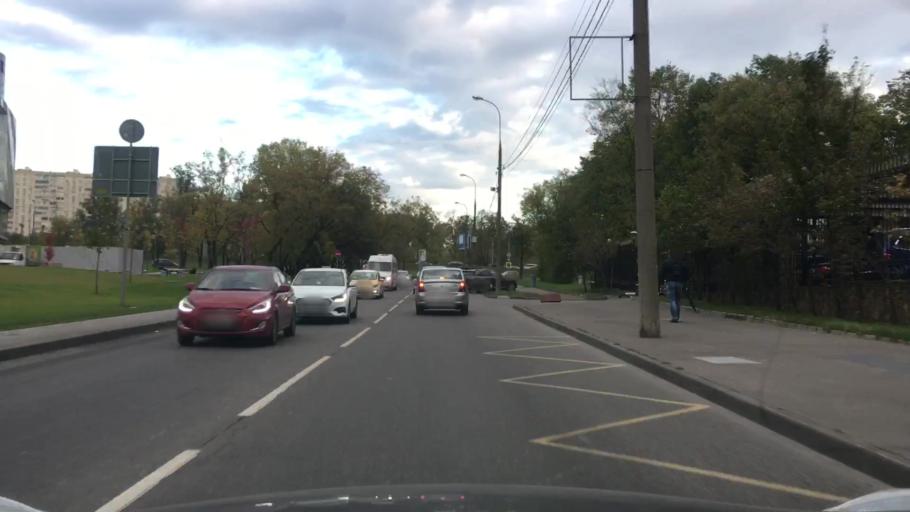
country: RU
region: Moscow
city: Davydkovo
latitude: 55.7274
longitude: 37.4789
